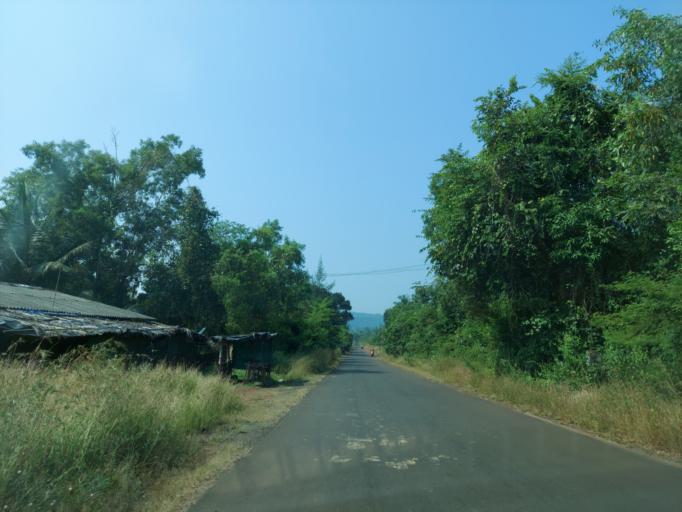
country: IN
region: Maharashtra
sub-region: Sindhudurg
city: Kudal
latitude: 15.9710
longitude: 73.6427
